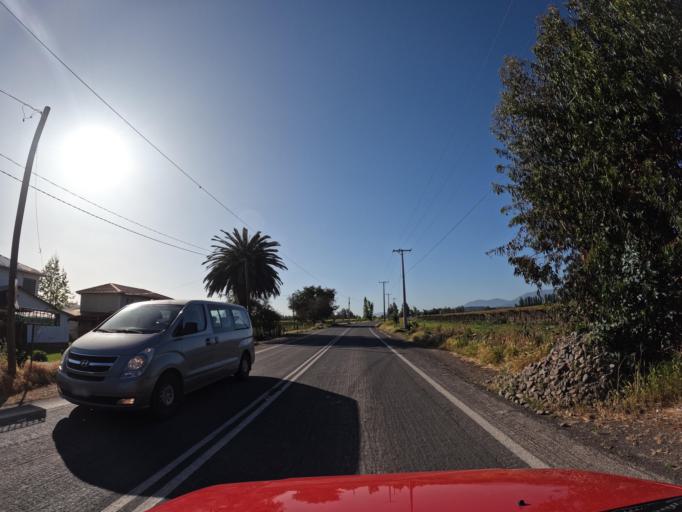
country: CL
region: Maule
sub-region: Provincia de Curico
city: Teno
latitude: -34.7662
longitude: -71.2366
